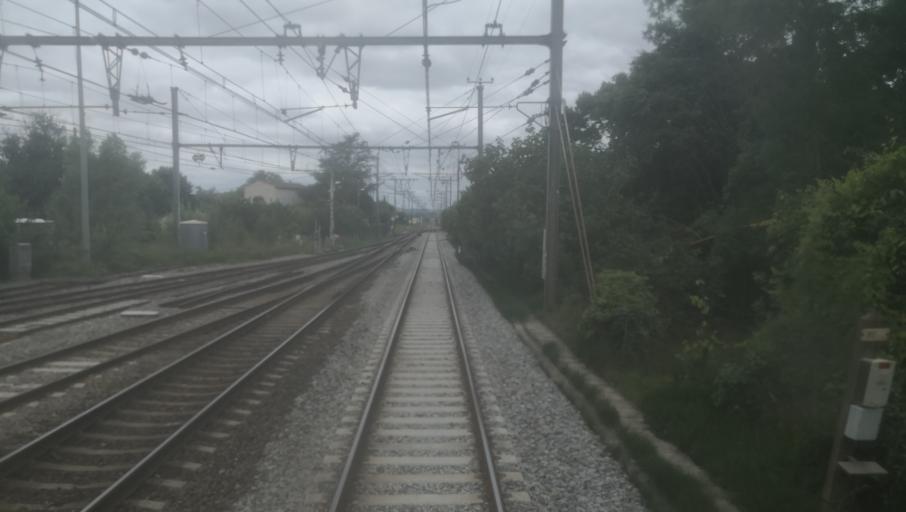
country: FR
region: Languedoc-Roussillon
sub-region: Departement de l'Aude
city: Castelnaudary
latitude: 43.3126
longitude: 1.9447
